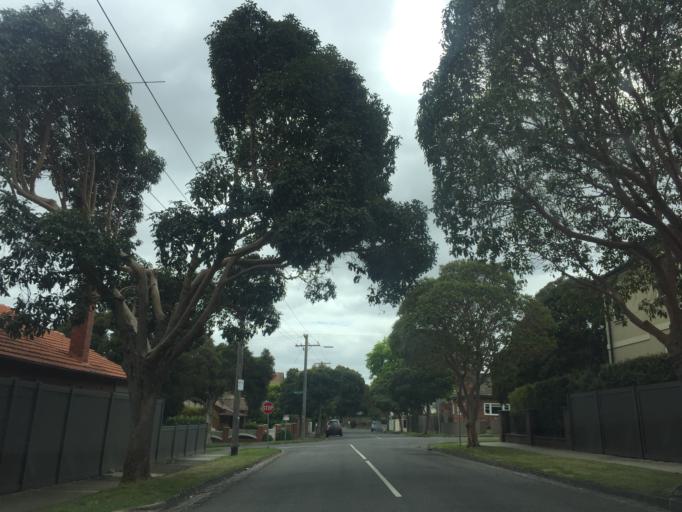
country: AU
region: Victoria
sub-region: Boroondara
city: Kew East
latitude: -37.8040
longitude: 145.0533
